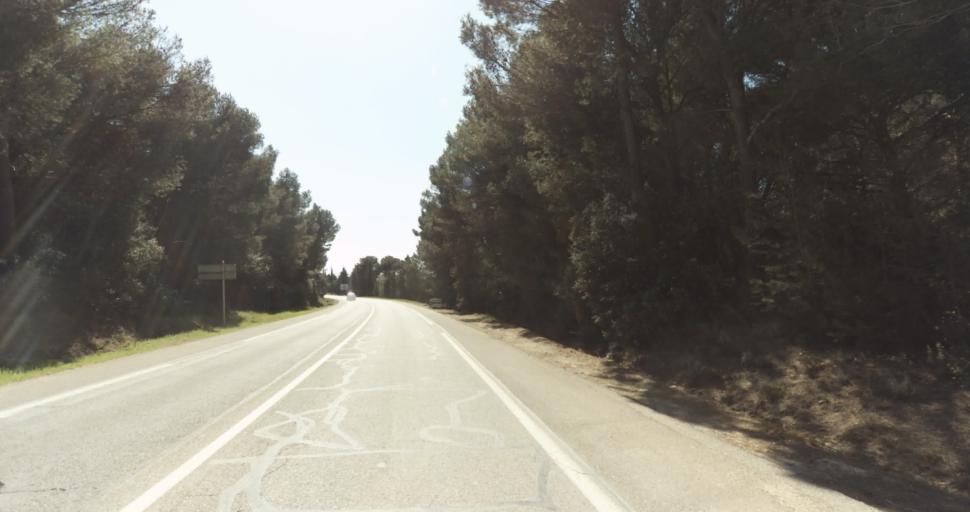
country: FR
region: Provence-Alpes-Cote d'Azur
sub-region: Departement des Bouches-du-Rhone
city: Pelissanne
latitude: 43.6329
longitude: 5.1668
